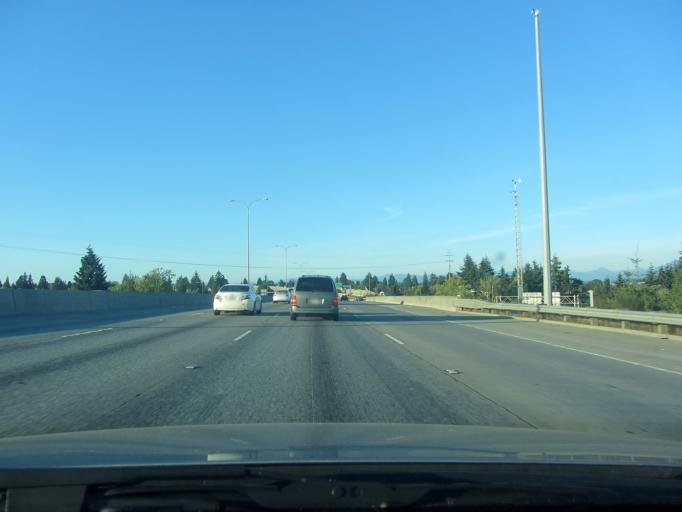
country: US
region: Washington
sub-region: Snohomish County
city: Everett
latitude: 47.9801
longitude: -122.1886
